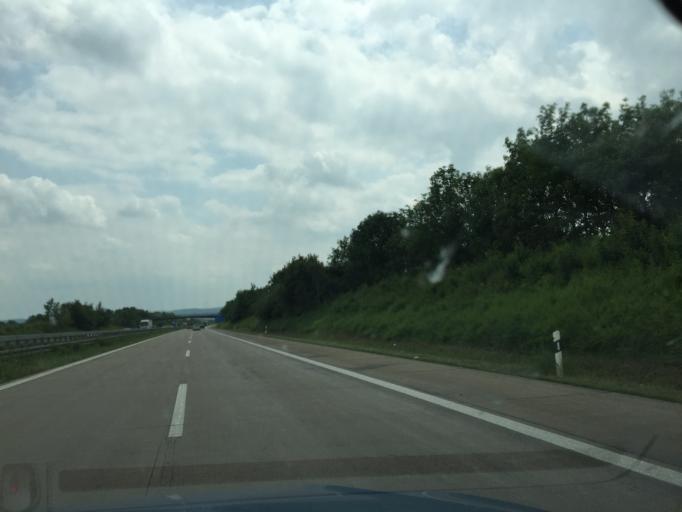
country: DE
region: Baden-Wuerttemberg
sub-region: Regierungsbezirk Stuttgart
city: Ellwangen
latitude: 48.9497
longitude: 10.1888
